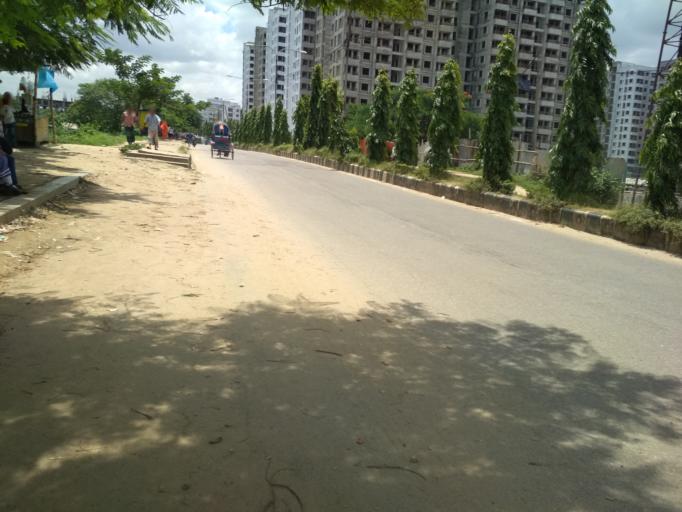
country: BD
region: Dhaka
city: Tungi
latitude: 23.8335
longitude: 90.3766
